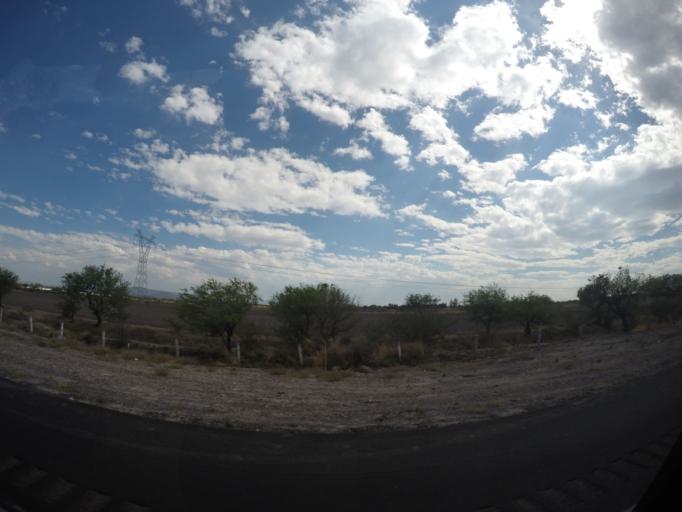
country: MX
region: Guanajuato
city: Santiago de Cuenda
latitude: 20.5803
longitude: -100.9885
